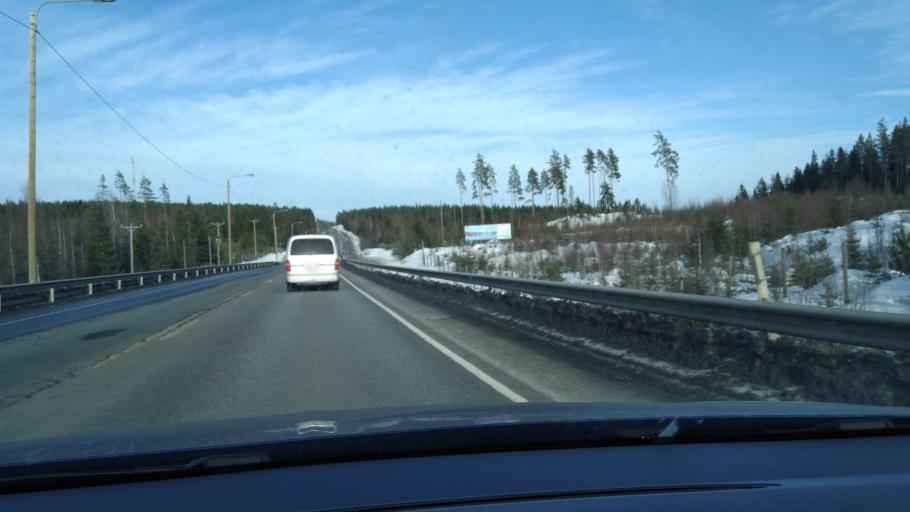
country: FI
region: Pirkanmaa
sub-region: Tampere
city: Orivesi
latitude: 61.6789
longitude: 24.3235
